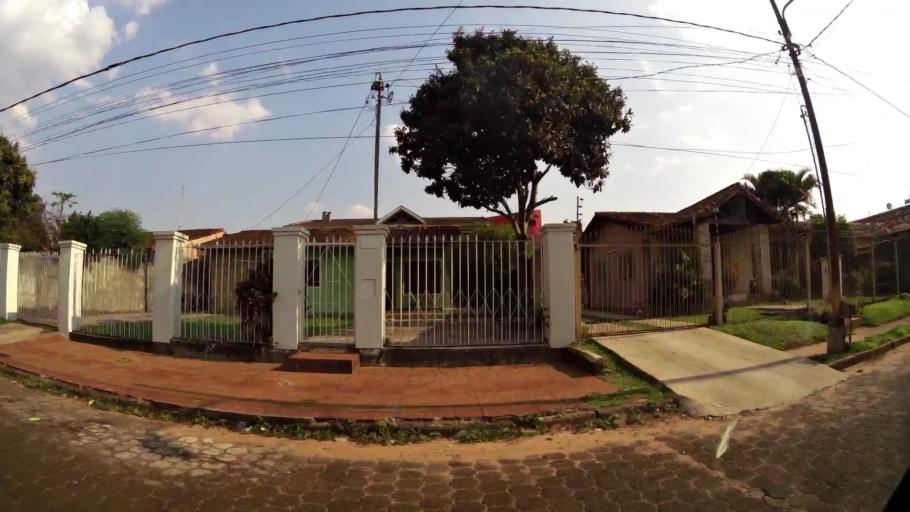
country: PY
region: Alto Parana
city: Presidente Franco
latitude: -25.5307
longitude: -54.6260
